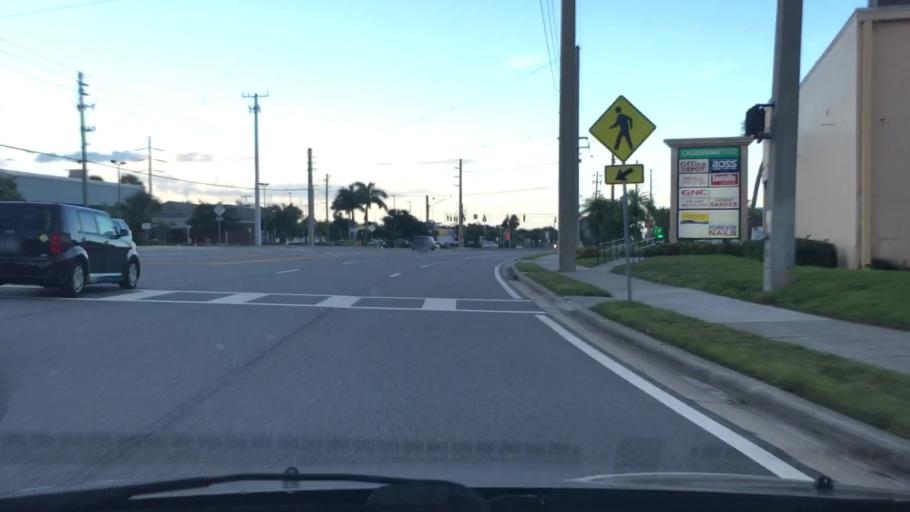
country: US
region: Florida
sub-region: Brevard County
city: Indian Harbour Beach
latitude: 28.1368
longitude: -80.5982
